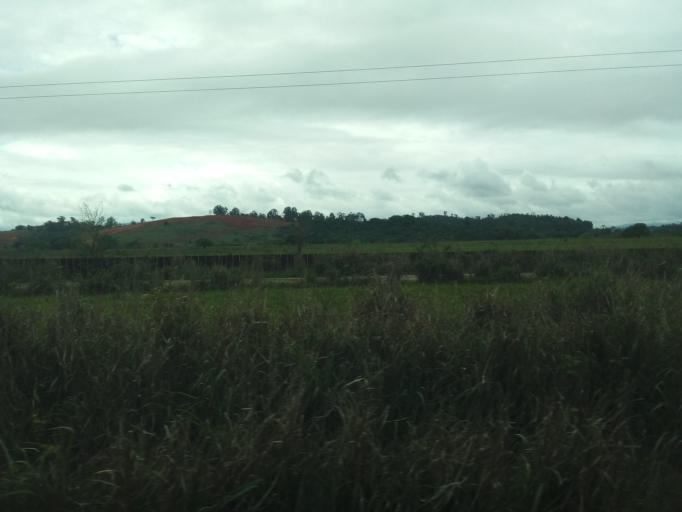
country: BR
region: Minas Gerais
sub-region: Ipatinga
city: Ipatinga
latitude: -19.4684
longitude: -42.4794
